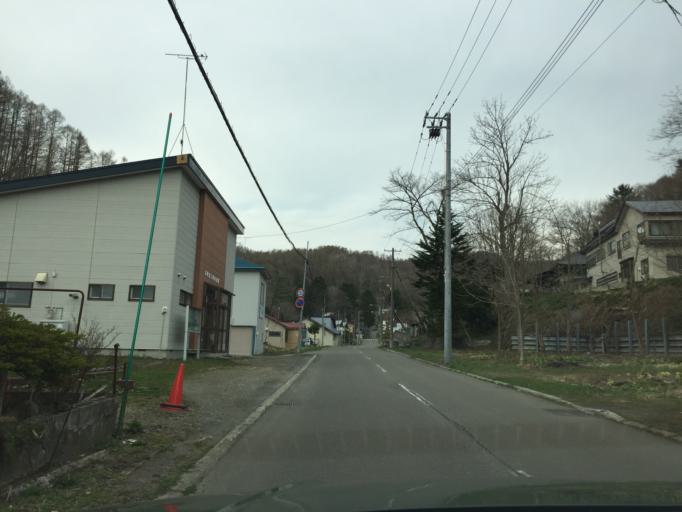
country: JP
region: Hokkaido
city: Utashinai
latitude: 43.5234
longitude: 142.0408
